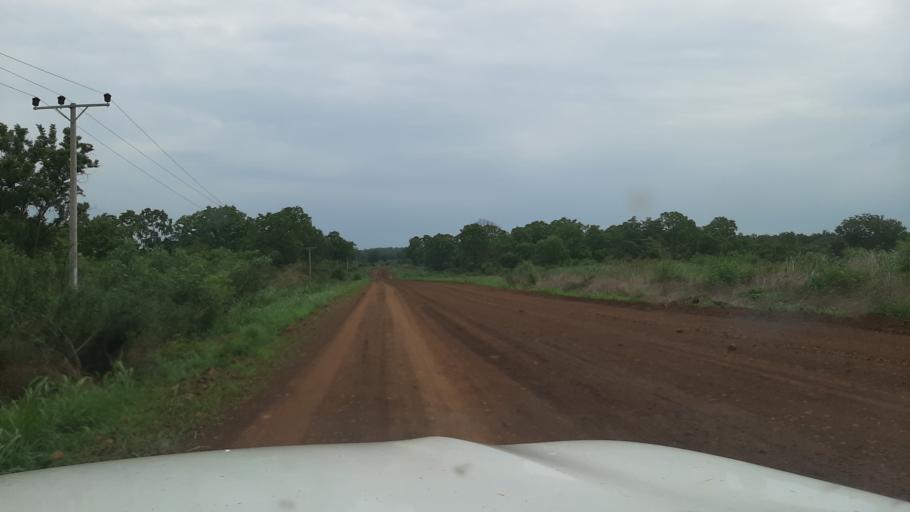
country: ET
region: Gambela
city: Gambela
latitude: 8.2080
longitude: 34.5157
